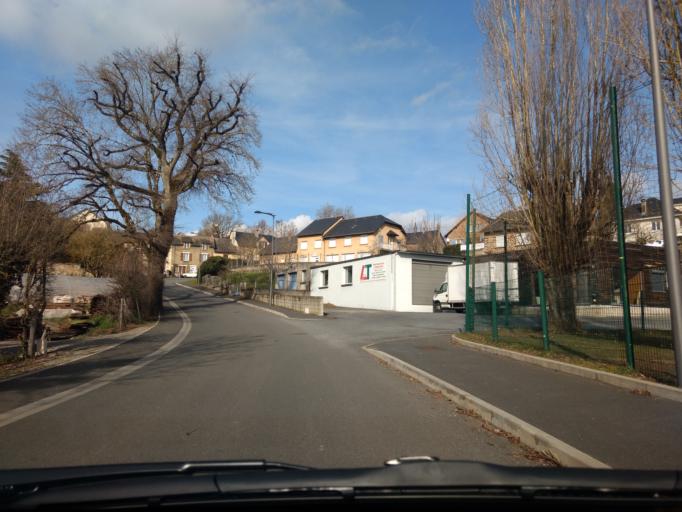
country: FR
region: Midi-Pyrenees
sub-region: Departement de l'Aveyron
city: Naucelle
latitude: 44.1950
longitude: 2.3405
